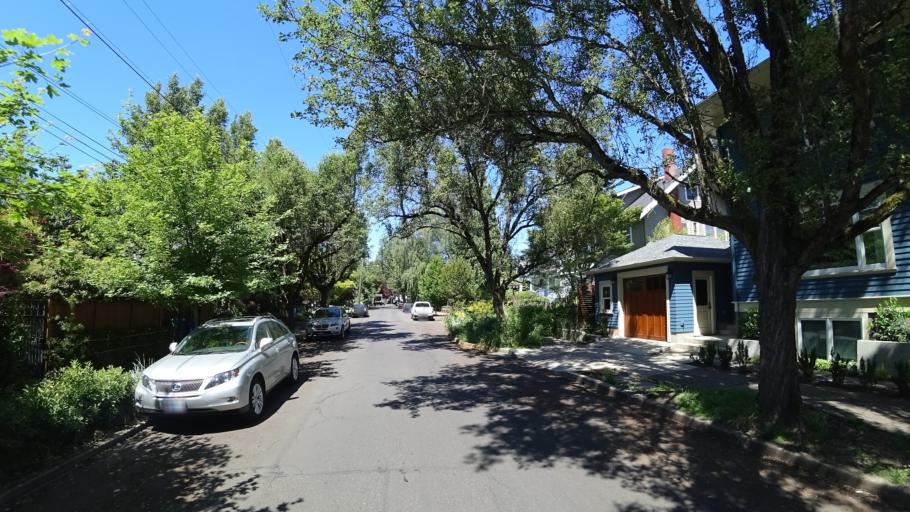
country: US
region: Oregon
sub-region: Multnomah County
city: Portland
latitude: 45.5087
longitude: -122.6394
